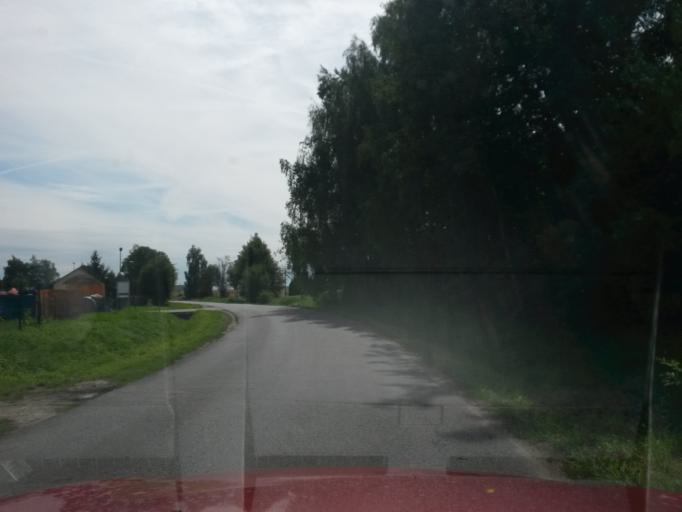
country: PL
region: Lesser Poland Voivodeship
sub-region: Powiat wielicki
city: Szarow
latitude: 49.9869
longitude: 20.2752
